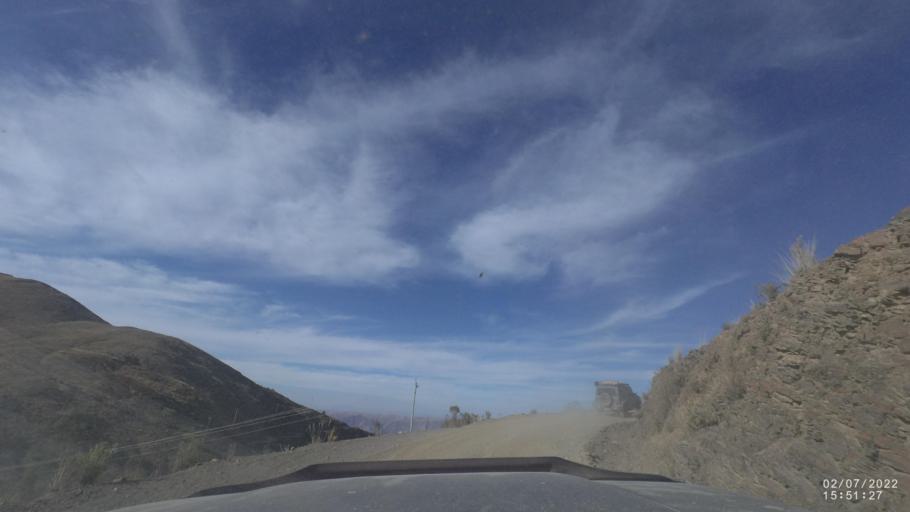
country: BO
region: Cochabamba
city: Irpa Irpa
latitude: -17.9046
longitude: -66.4138
